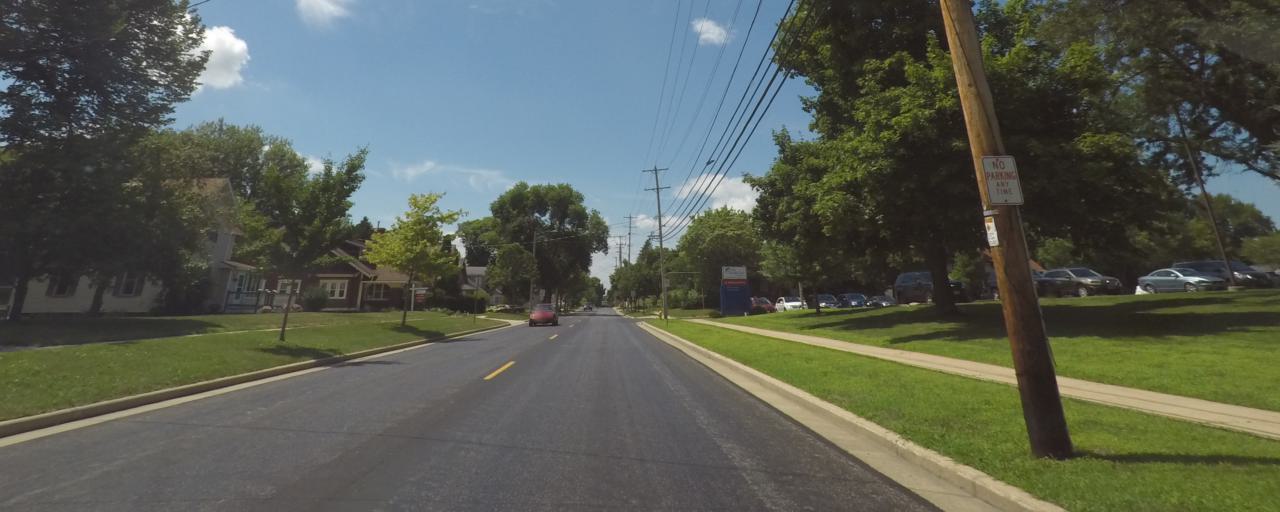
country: US
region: Wisconsin
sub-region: Jefferson County
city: Fort Atkinson
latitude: 42.9301
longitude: -88.8280
